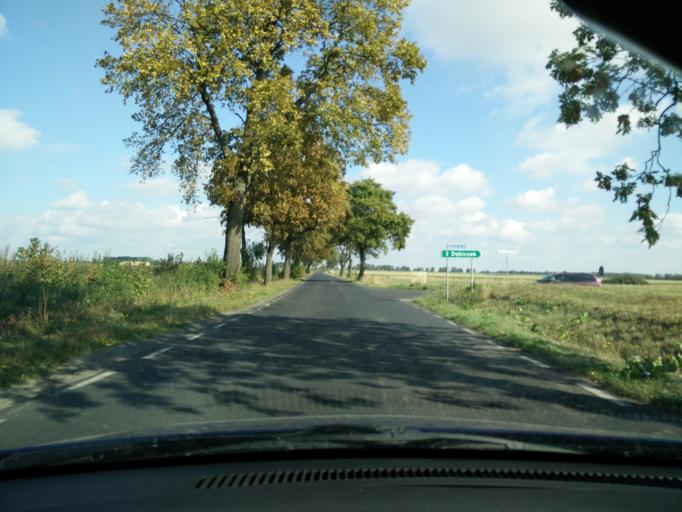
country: PL
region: Greater Poland Voivodeship
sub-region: Powiat sredzki
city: Dominowo
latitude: 52.2695
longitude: 17.3153
